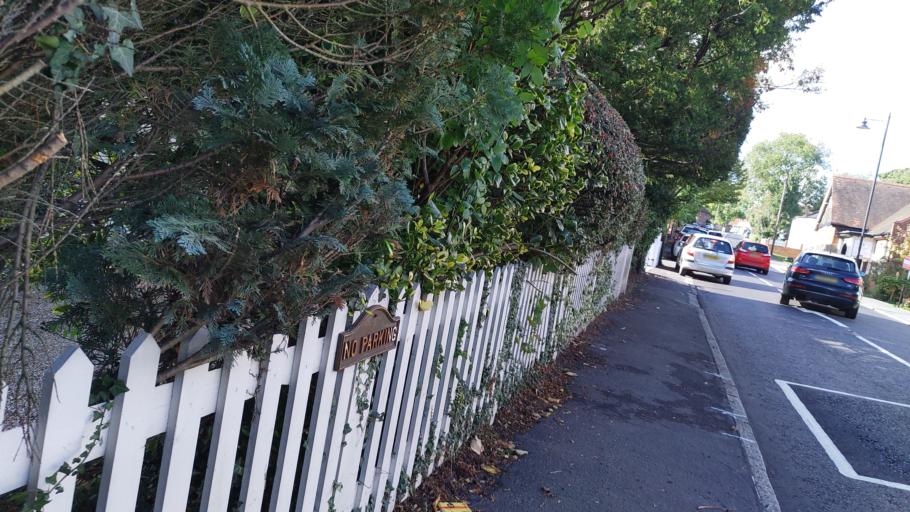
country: GB
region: England
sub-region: Hertfordshire
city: Potters Bar
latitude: 51.7035
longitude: -0.1481
